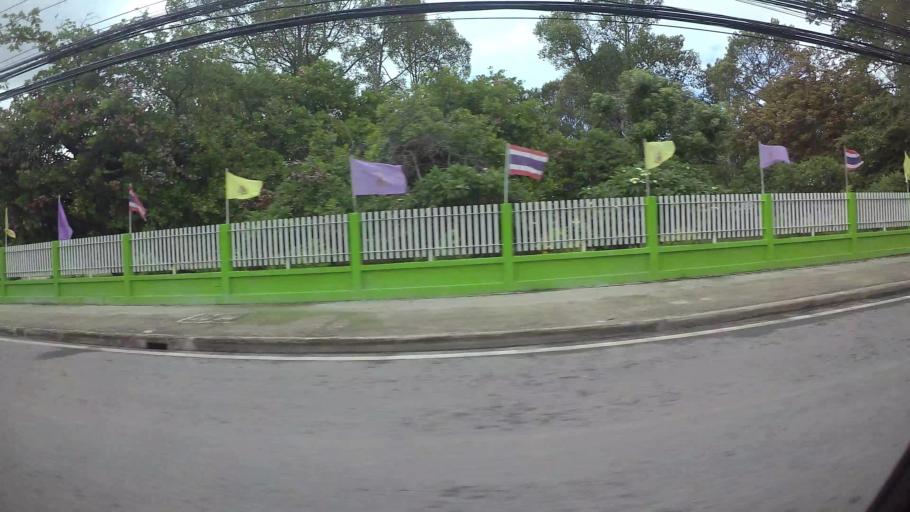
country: TH
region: Rayong
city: Rayong
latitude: 12.6834
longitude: 101.2276
